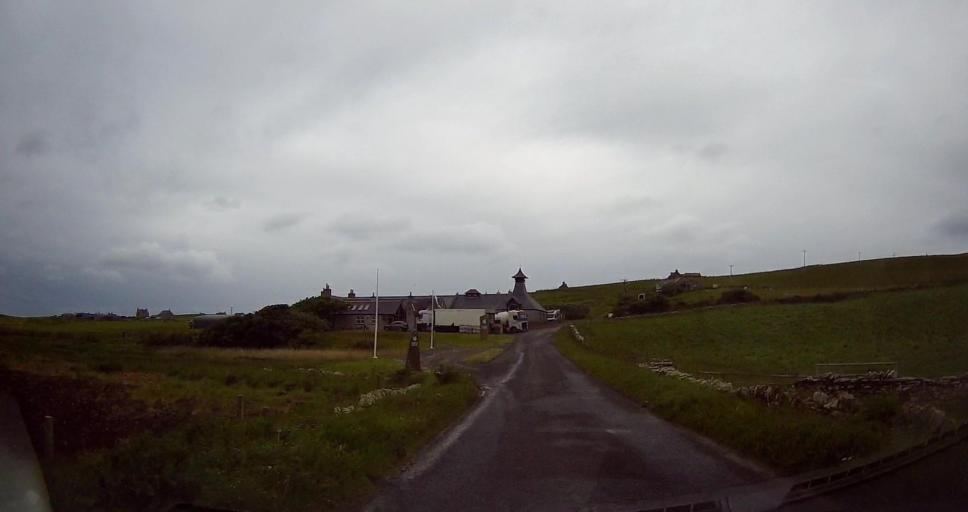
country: GB
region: Scotland
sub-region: Orkney Islands
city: Stromness
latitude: 59.0692
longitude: -3.3073
